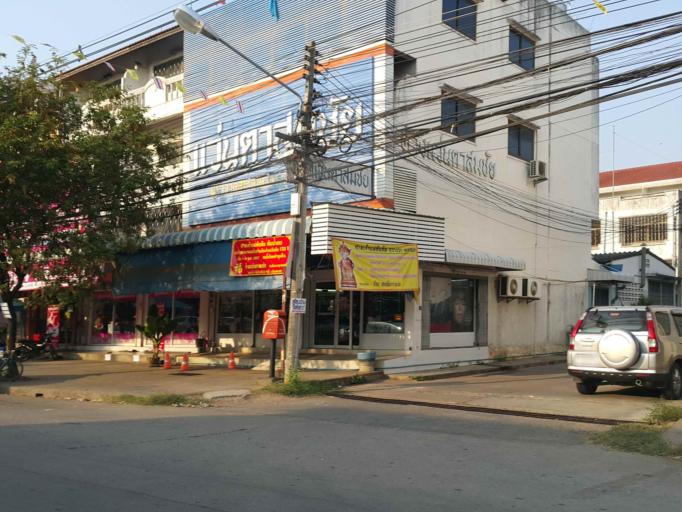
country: TH
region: Sukhothai
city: Sawankhalok
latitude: 17.3107
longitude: 99.8307
